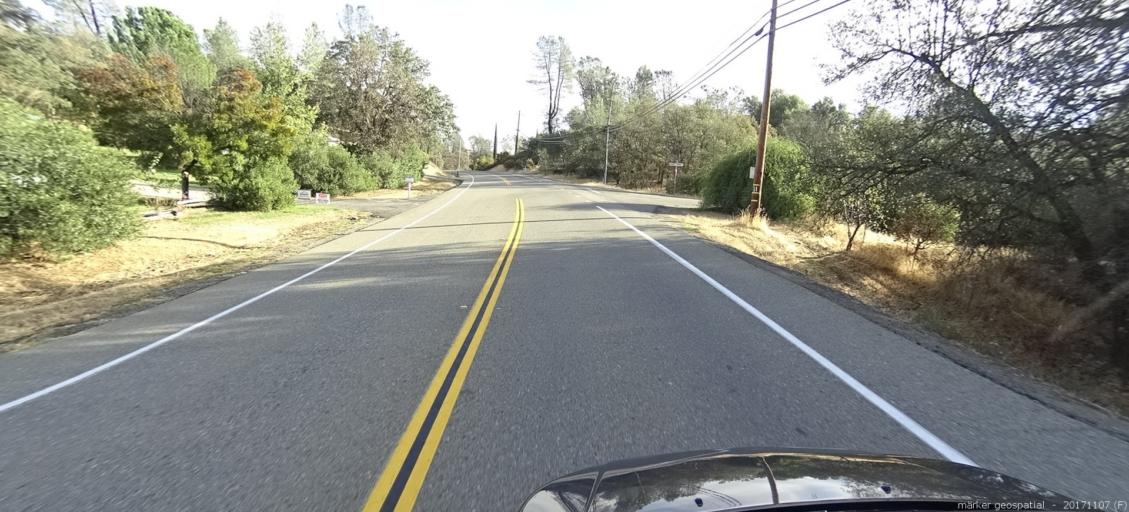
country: US
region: California
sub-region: Shasta County
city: Shasta
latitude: 40.5469
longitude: -122.4581
